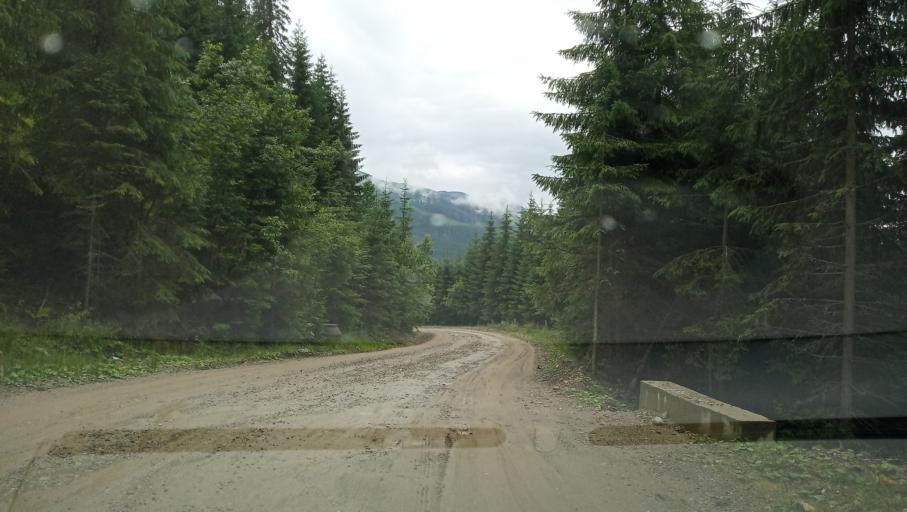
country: RO
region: Hunedoara
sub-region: Oras Petrila
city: Petrila
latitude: 45.4032
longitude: 23.5741
